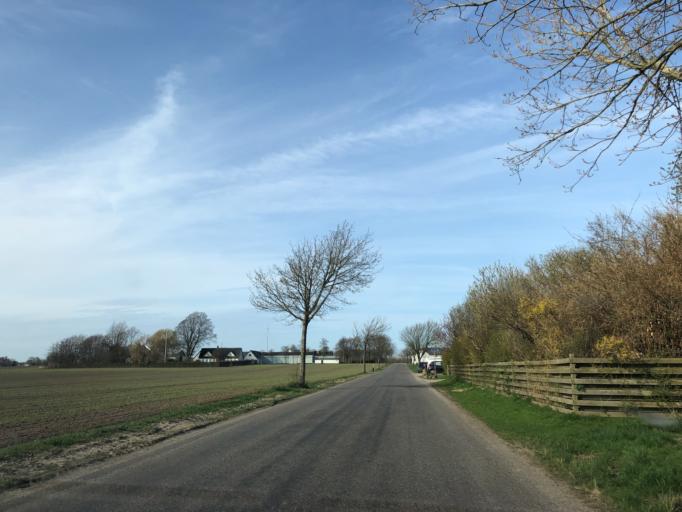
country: DK
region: Zealand
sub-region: Stevns Kommune
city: Store Heddinge
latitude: 55.2887
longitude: 12.4445
